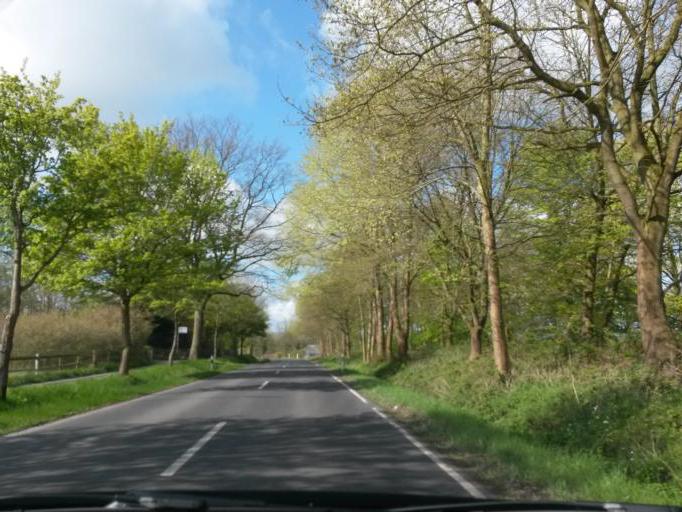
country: DE
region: Schleswig-Holstein
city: Holm
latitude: 53.6200
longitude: 9.6660
